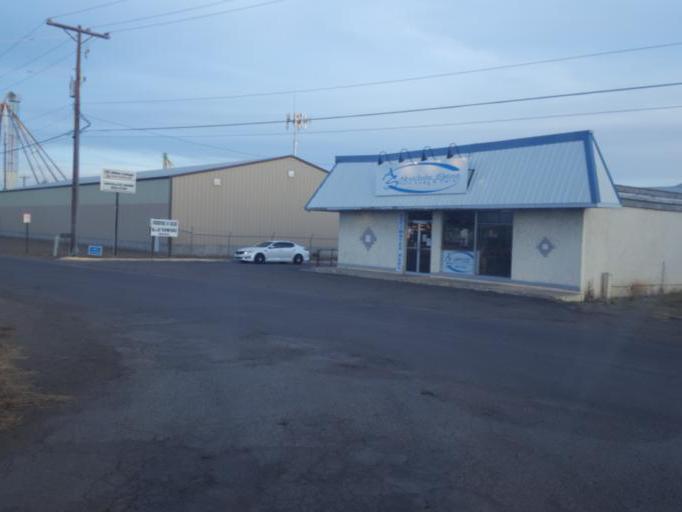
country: US
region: Colorado
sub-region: Rio Grande County
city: Monte Vista
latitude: 37.5818
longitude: -106.1467
